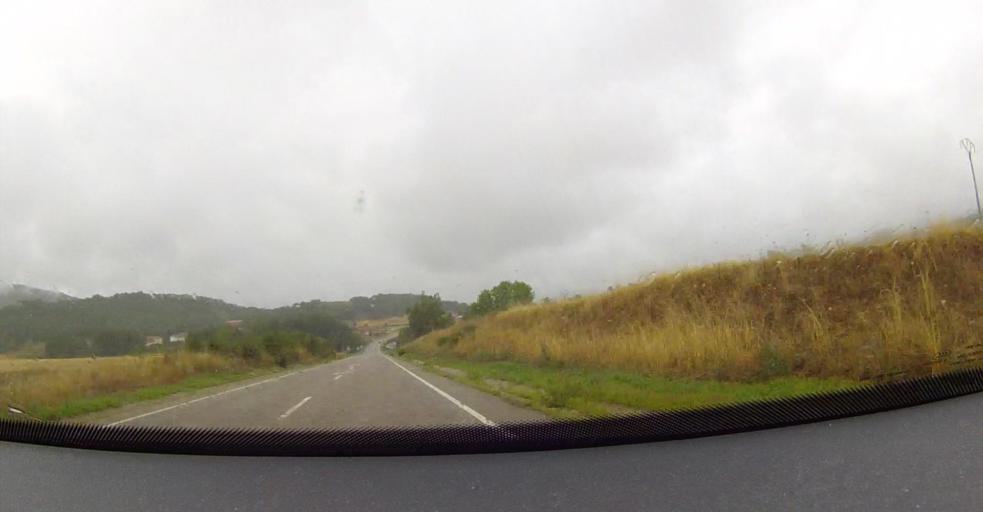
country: ES
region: Castille and Leon
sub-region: Provincia de Leon
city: Bonar
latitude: 42.8394
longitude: -5.2449
